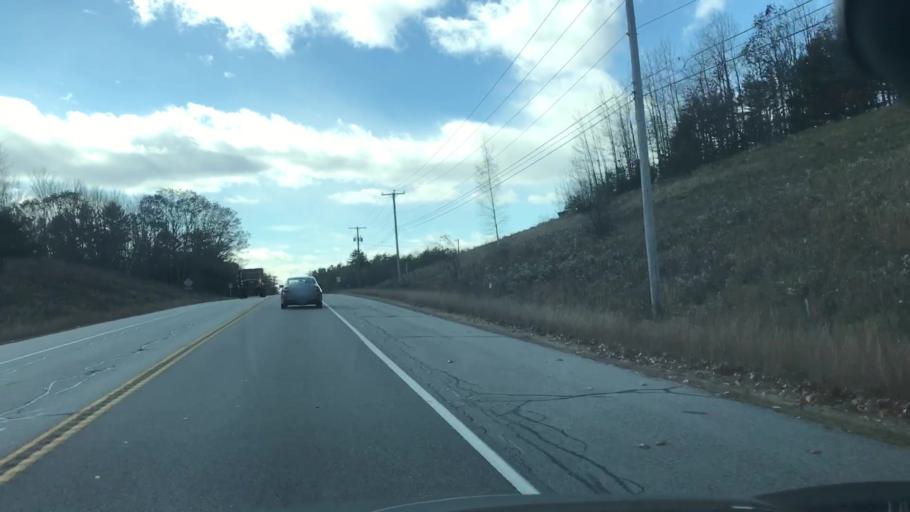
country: US
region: New Hampshire
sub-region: Merrimack County
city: Pittsfield
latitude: 43.3054
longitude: -71.3395
